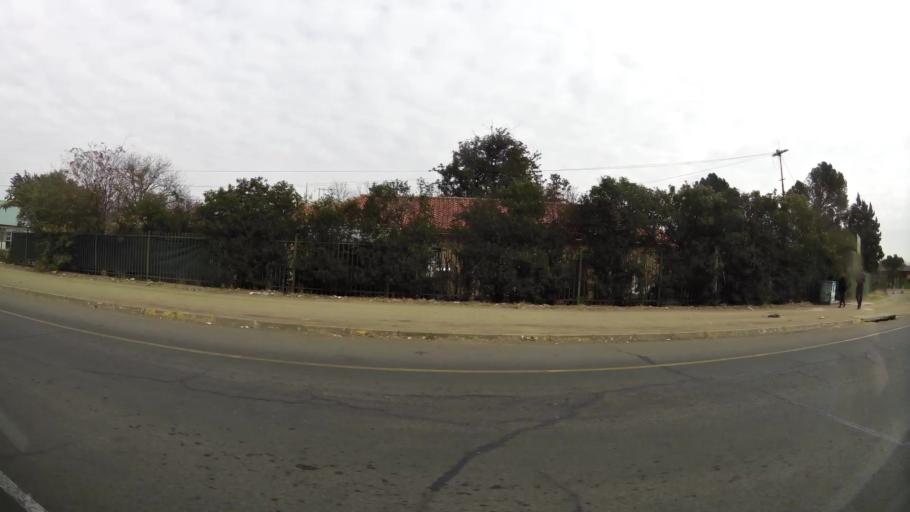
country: ZA
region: Orange Free State
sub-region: Mangaung Metropolitan Municipality
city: Bloemfontein
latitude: -29.1275
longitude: 26.2084
